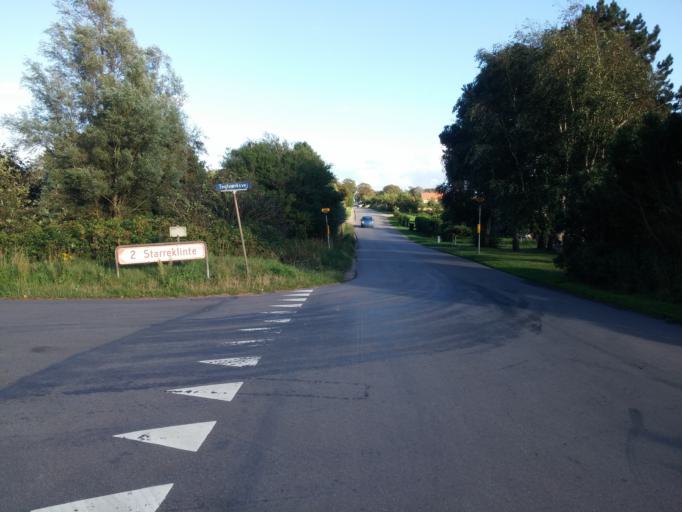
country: DK
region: Zealand
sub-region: Odsherred Kommune
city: Horve
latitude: 55.7590
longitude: 11.3542
